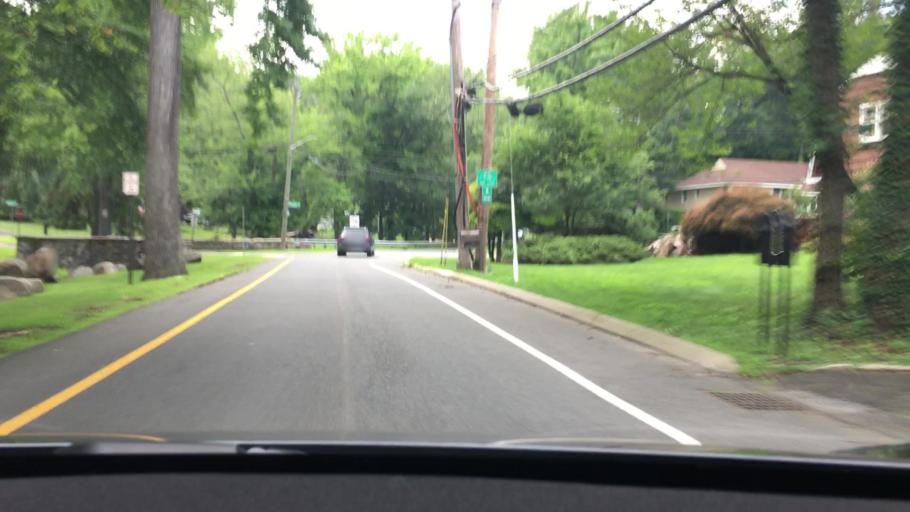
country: US
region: New York
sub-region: Westchester County
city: New Rochelle
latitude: 40.9361
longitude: -73.7789
